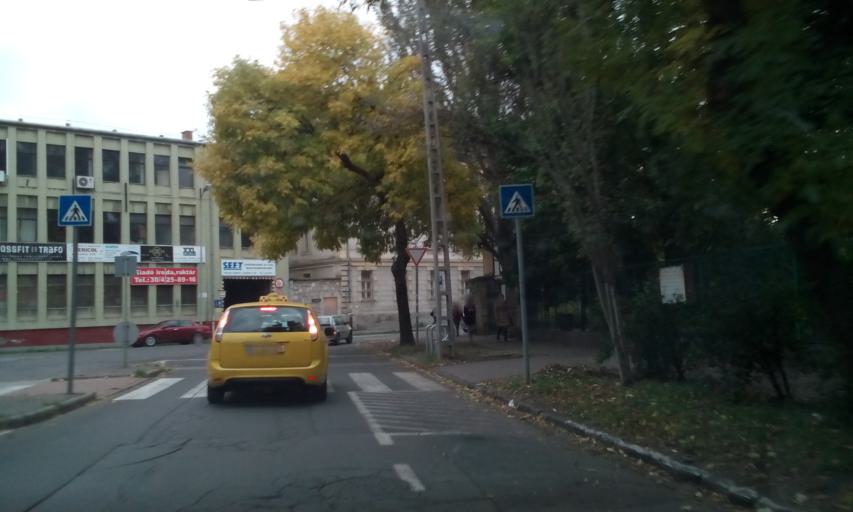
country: HU
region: Budapest
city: Budapest VIII. keruelet
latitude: 47.4841
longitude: 19.0856
